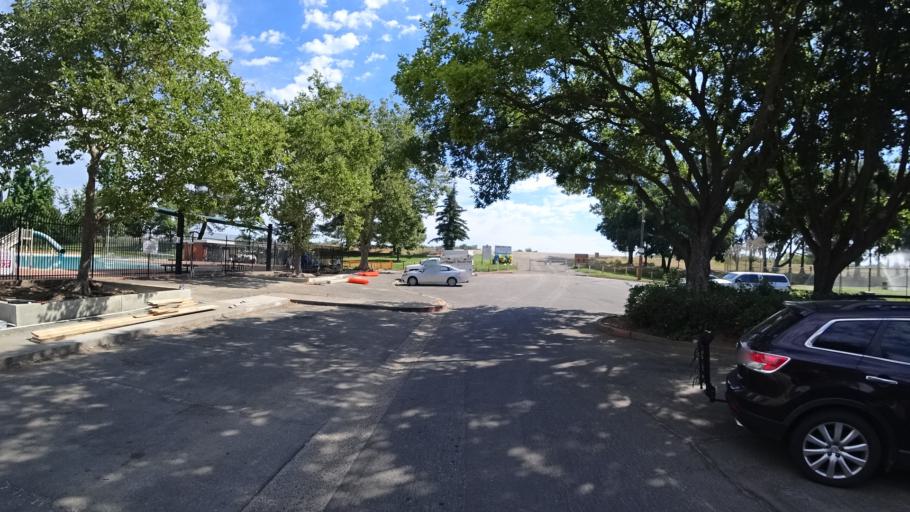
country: US
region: California
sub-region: Sacramento County
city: Arden-Arcade
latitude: 38.5795
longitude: -121.4260
